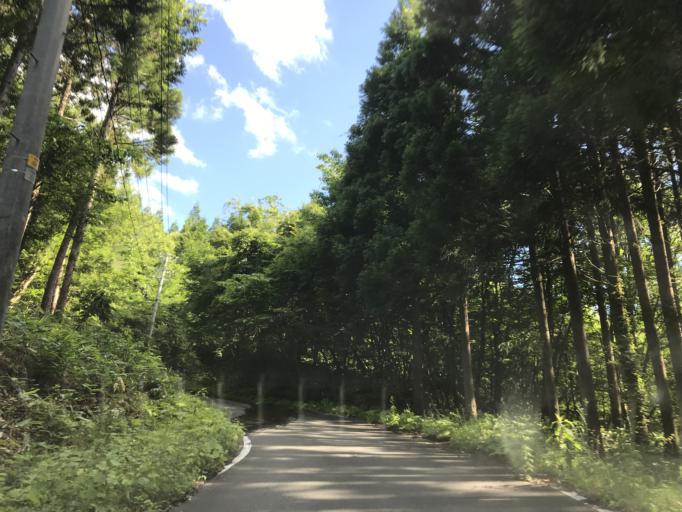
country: JP
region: Iwate
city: Ichinoseki
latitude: 38.8933
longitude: 140.9068
